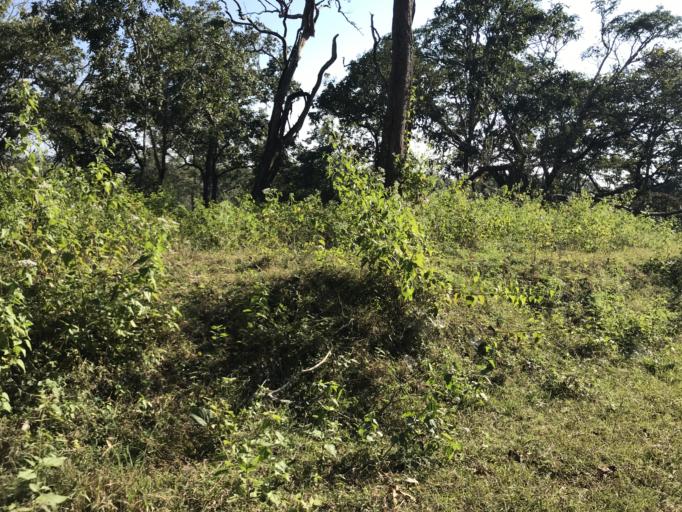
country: IN
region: Karnataka
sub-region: Mysore
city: Heggadadevankote
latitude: 11.9553
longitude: 76.2299
